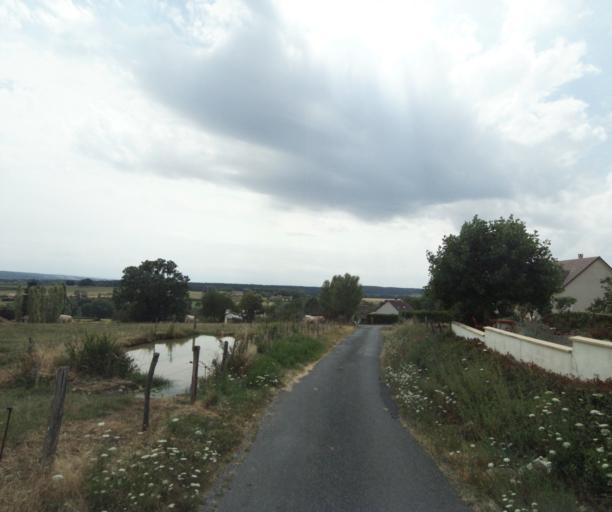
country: FR
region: Bourgogne
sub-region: Departement de Saone-et-Loire
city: Gueugnon
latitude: 46.5994
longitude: 4.0219
